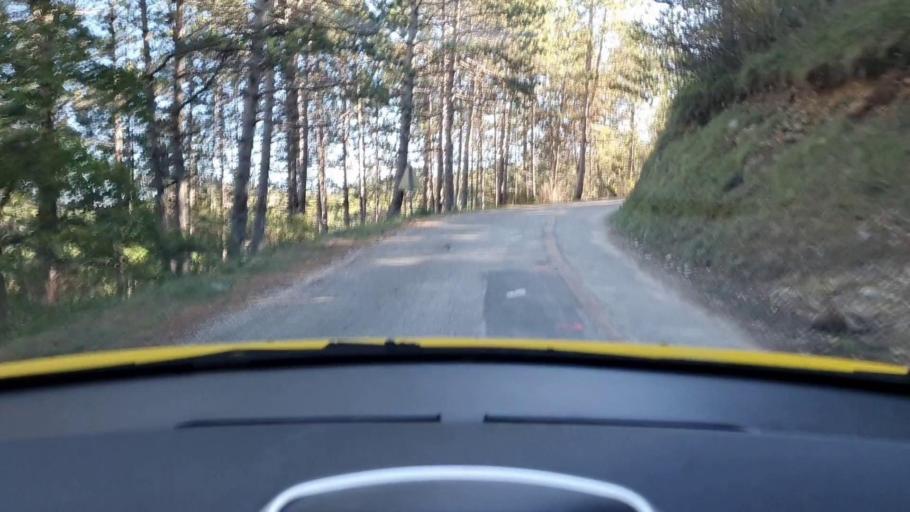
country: FR
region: Languedoc-Roussillon
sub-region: Departement du Gard
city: Aveze
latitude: 43.9626
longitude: 3.4310
